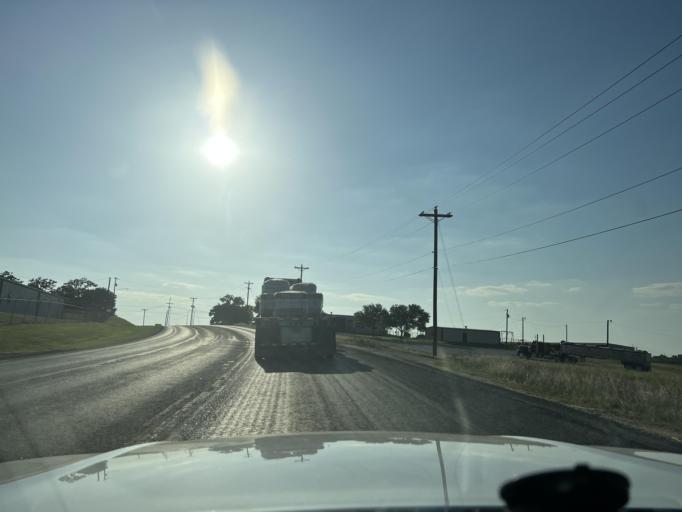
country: US
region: Texas
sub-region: Washington County
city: Brenham
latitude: 30.1787
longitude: -96.3856
